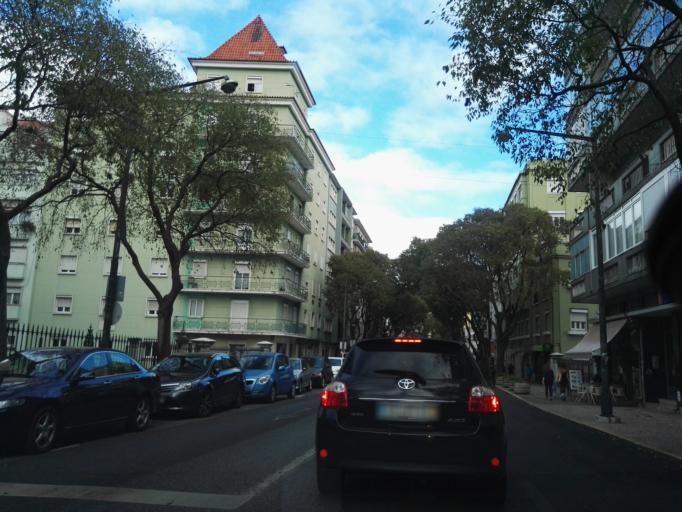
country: PT
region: Lisbon
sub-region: Lisbon
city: Lisbon
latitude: 38.7313
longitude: -9.1368
